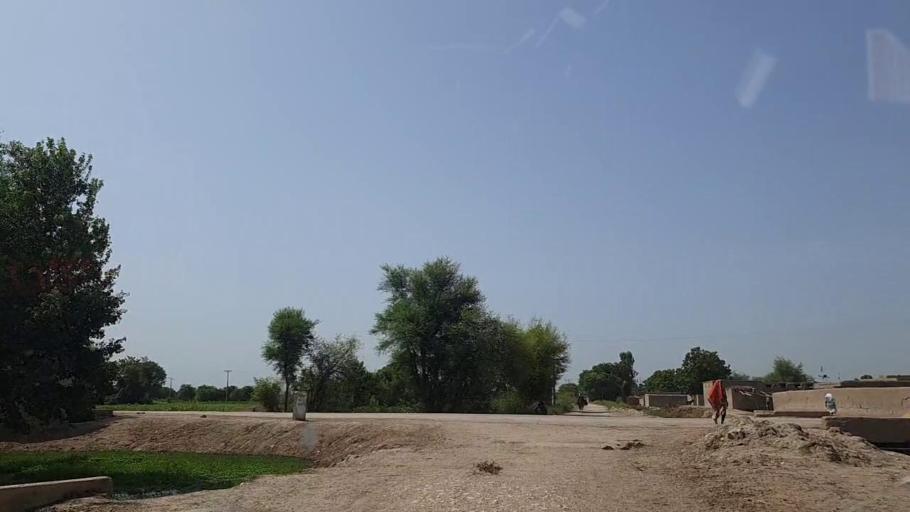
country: PK
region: Sindh
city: Naushahro Firoz
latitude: 26.8523
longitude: 68.0278
